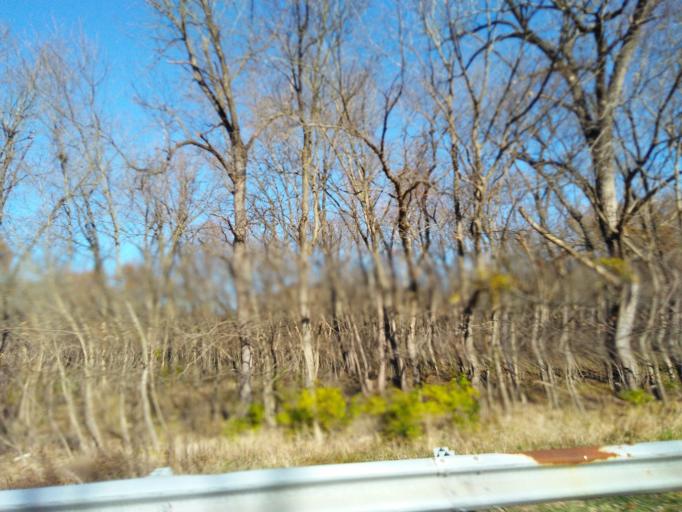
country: US
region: Illinois
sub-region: Madison County
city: Saint Jacob
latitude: 38.7162
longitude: -89.8075
